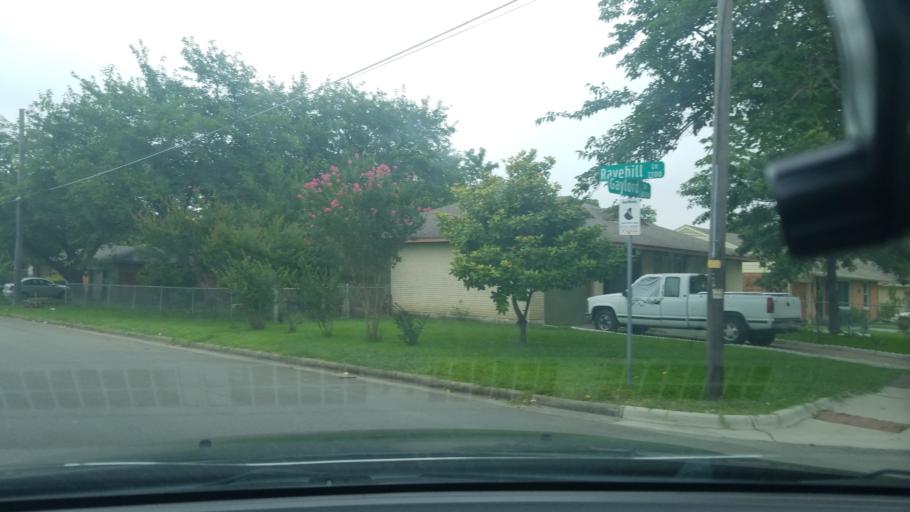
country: US
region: Texas
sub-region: Dallas County
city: Balch Springs
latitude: 32.7528
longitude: -96.6906
